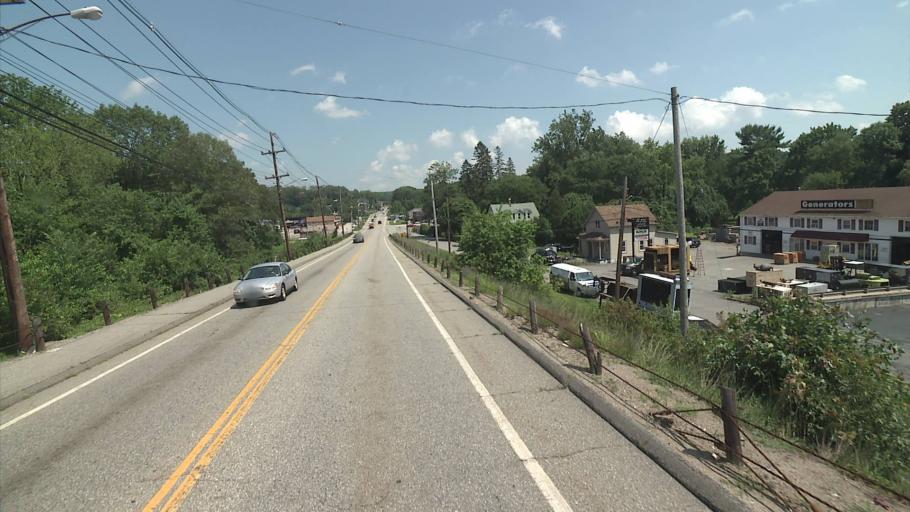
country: US
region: Connecticut
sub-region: New London County
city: Norwich
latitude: 41.5579
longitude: -72.1173
